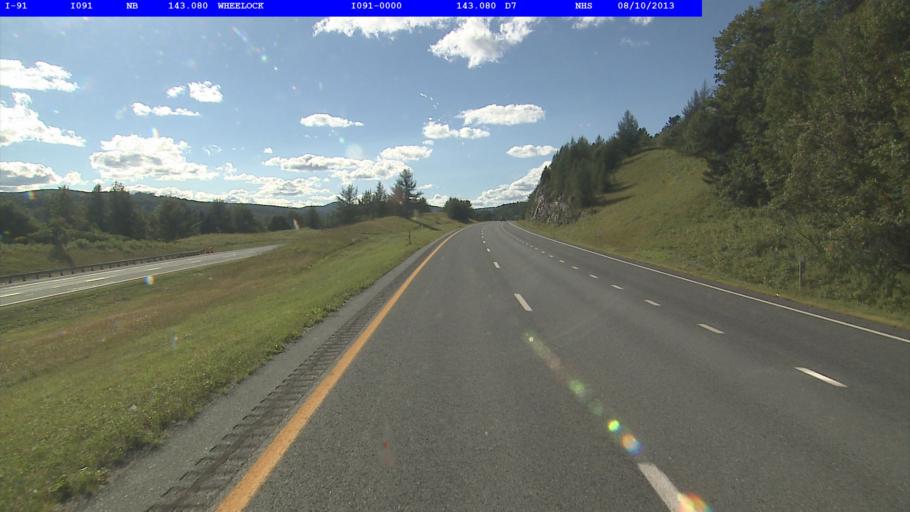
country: US
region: Vermont
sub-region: Caledonia County
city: Lyndonville
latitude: 44.5843
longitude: -72.0685
